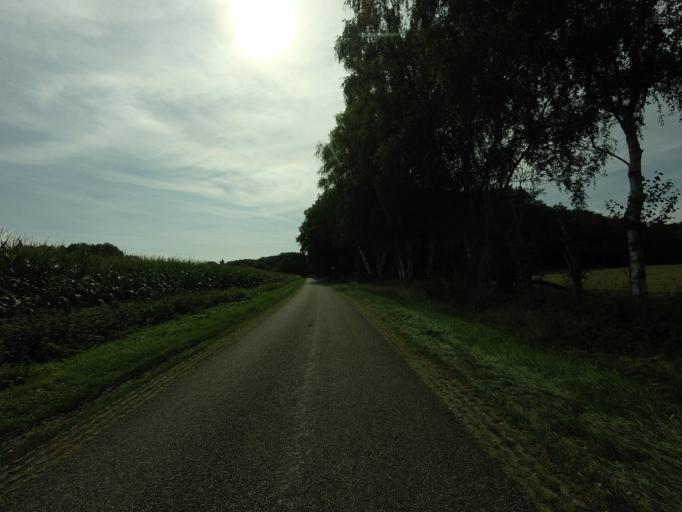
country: NL
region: Drenthe
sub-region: Gemeente Borger-Odoorn
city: Borger
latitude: 52.9092
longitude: 6.7028
